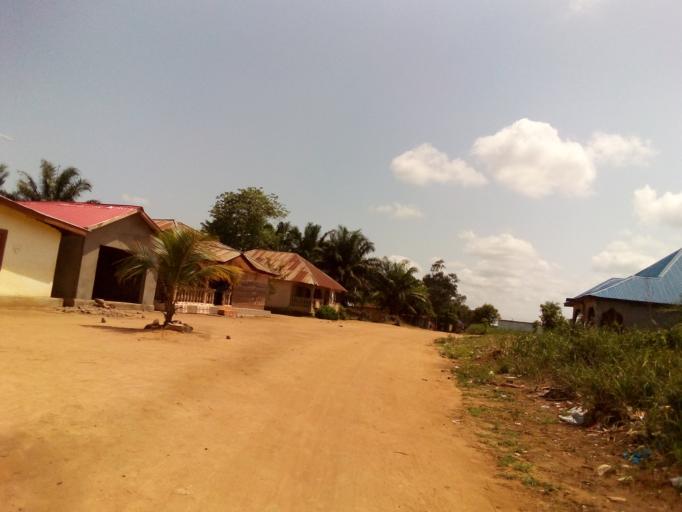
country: SL
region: Western Area
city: Waterloo
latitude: 8.3495
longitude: -13.0182
